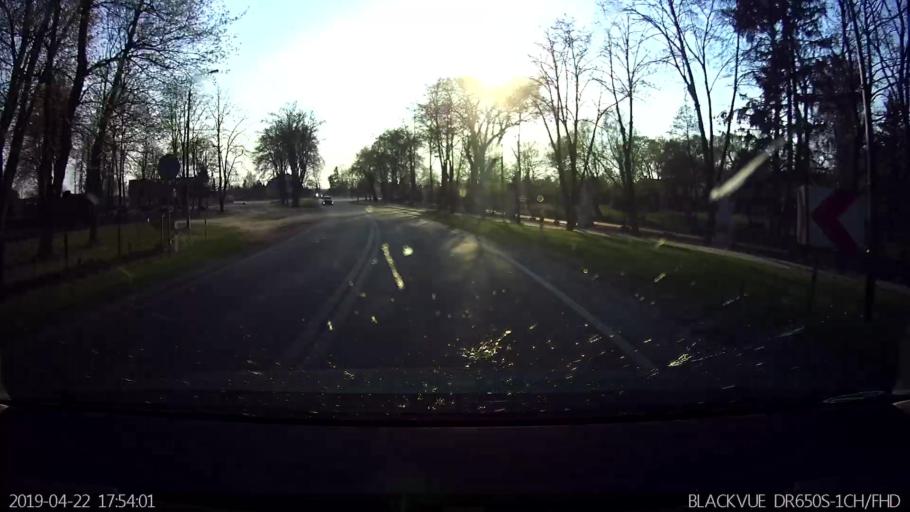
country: PL
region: Masovian Voivodeship
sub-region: Powiat wegrowski
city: Liw
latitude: 52.4566
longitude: 21.9458
